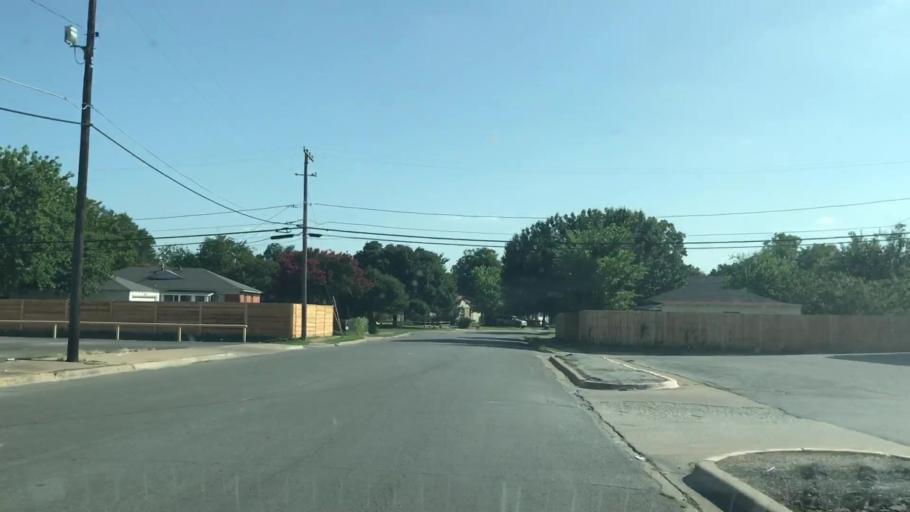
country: US
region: Texas
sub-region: Dallas County
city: Garland
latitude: 32.8343
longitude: -96.6762
